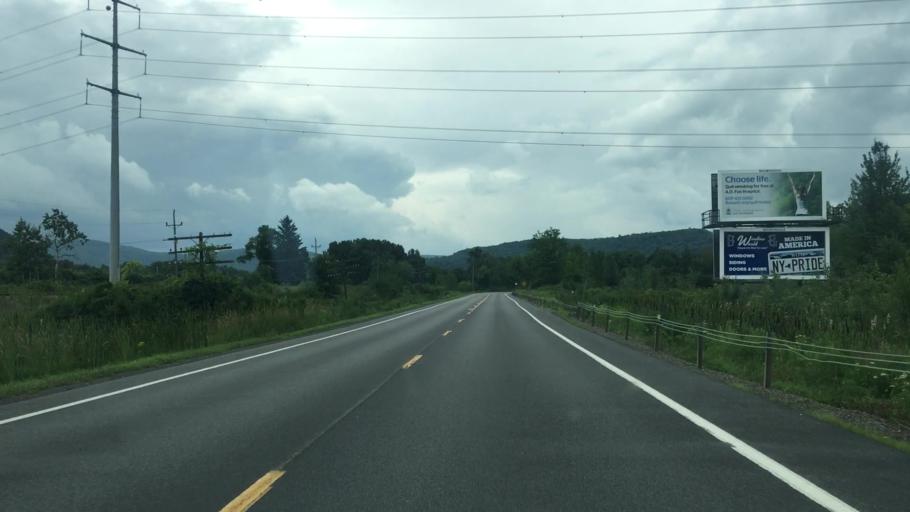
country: US
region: New York
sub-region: Otsego County
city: Otego
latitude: 42.4270
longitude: -75.1328
